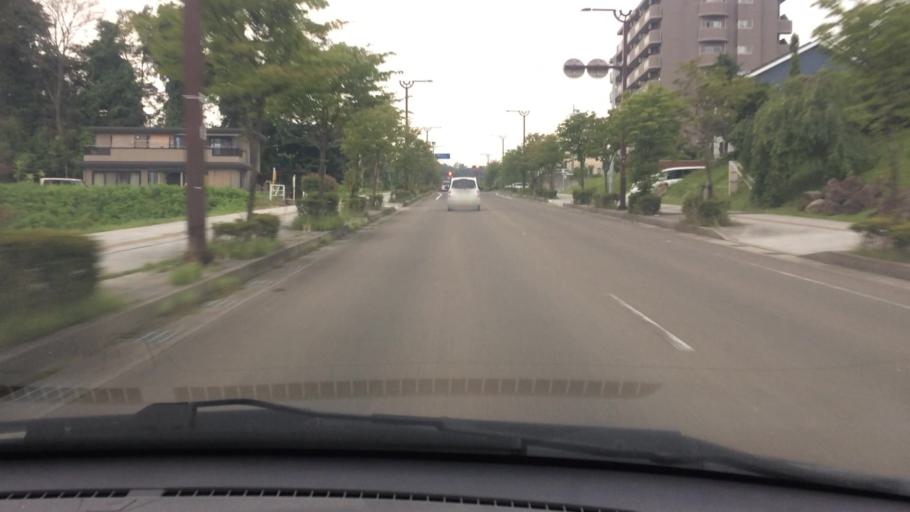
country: JP
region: Miyagi
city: Rifu
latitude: 38.3283
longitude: 140.9572
